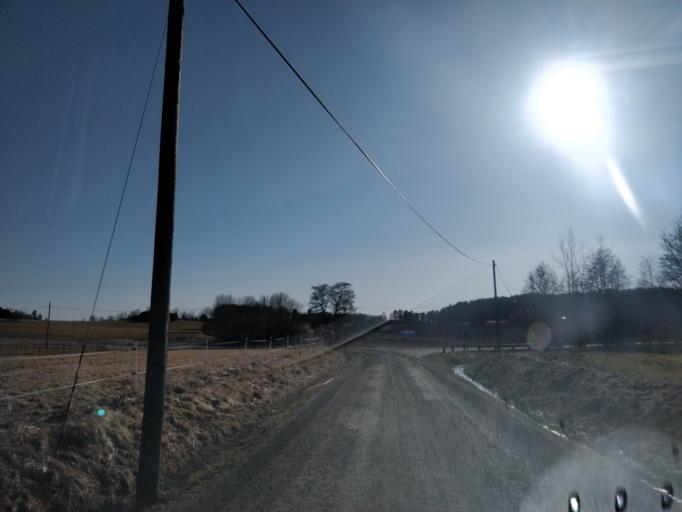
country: SE
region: Uppsala
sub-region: Enkopings Kommun
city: Enkoping
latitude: 59.8142
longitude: 17.1186
